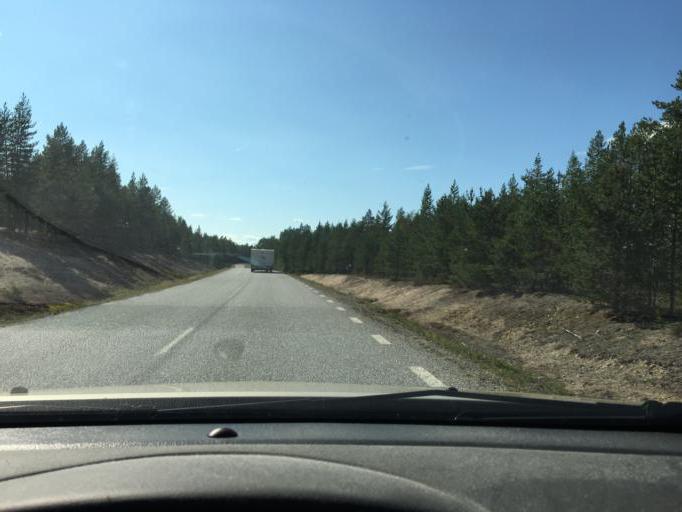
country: SE
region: Norrbotten
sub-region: Lulea Kommun
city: Ranea
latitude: 66.0488
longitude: 22.2498
